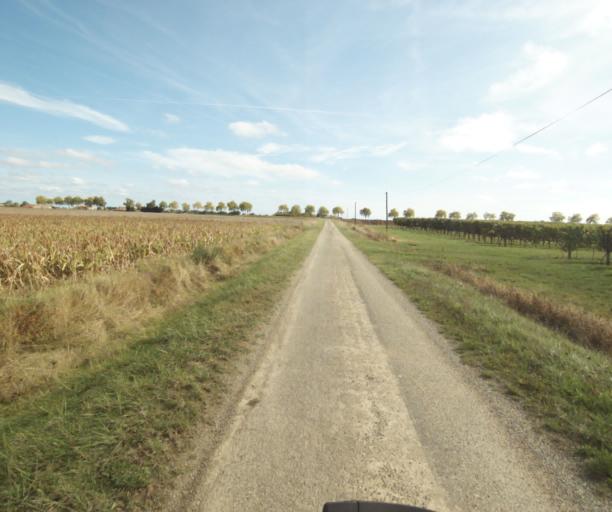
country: FR
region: Midi-Pyrenees
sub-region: Departement du Tarn-et-Garonne
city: Saint-Porquier
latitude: 43.9479
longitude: 1.1414
